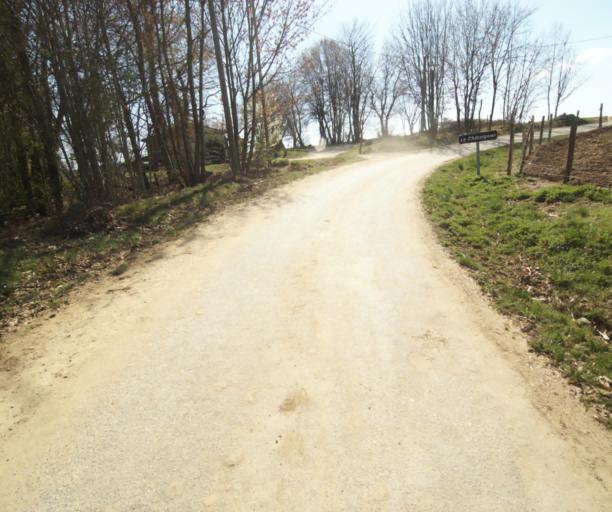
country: FR
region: Limousin
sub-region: Departement de la Correze
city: Saint-Mexant
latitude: 45.2900
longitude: 1.6853
